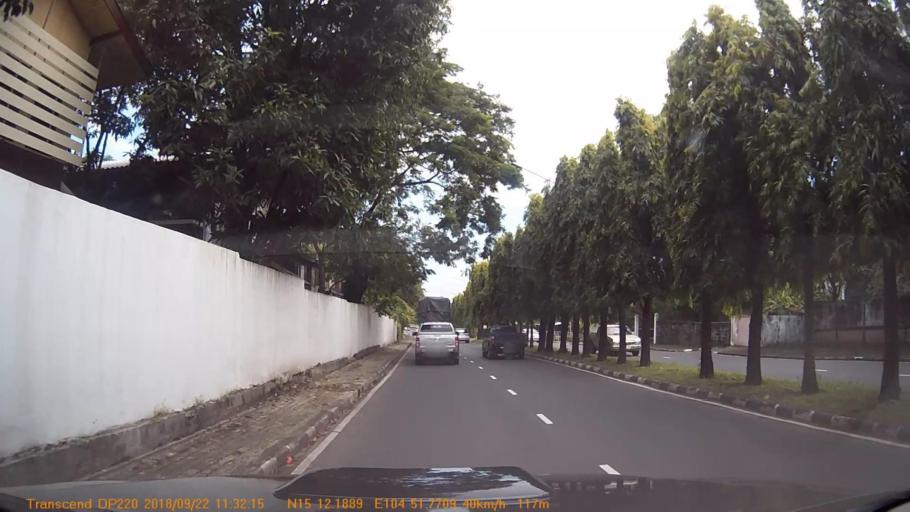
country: TH
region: Changwat Ubon Ratchathani
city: Warin Chamrap
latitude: 15.2031
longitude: 104.8628
